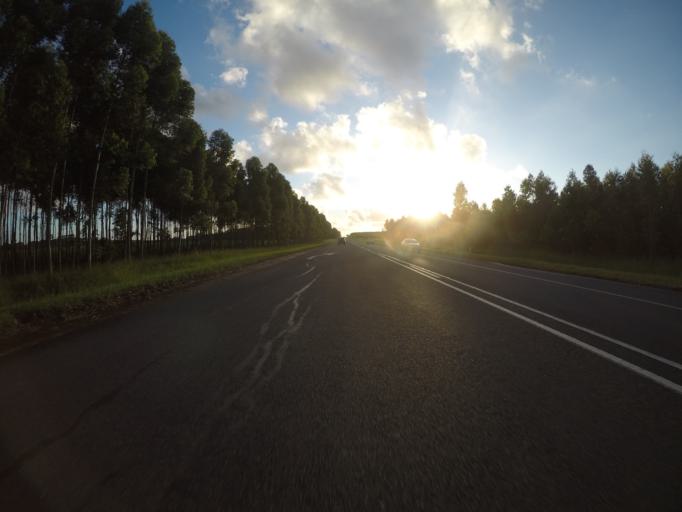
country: ZA
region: KwaZulu-Natal
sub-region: uThungulu District Municipality
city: Richards Bay
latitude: -28.6953
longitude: 31.9832
